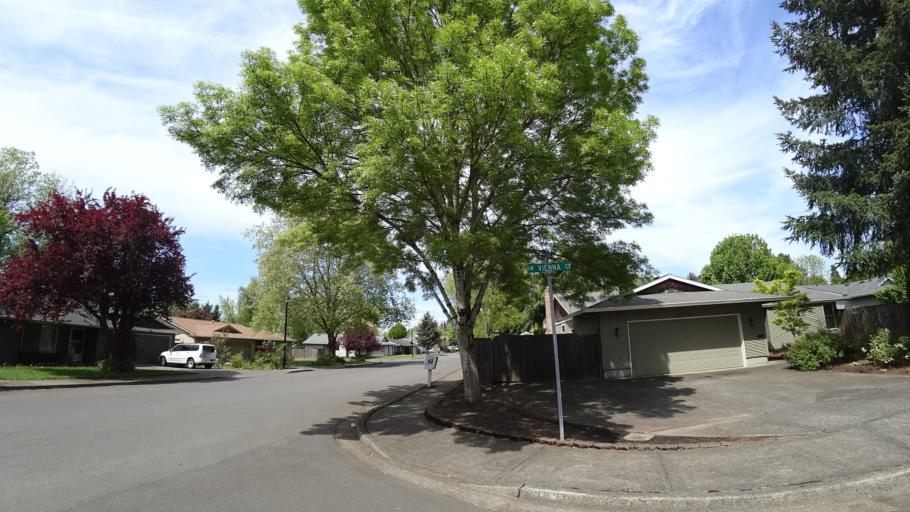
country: US
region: Oregon
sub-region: Washington County
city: Aloha
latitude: 45.4691
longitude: -122.8874
